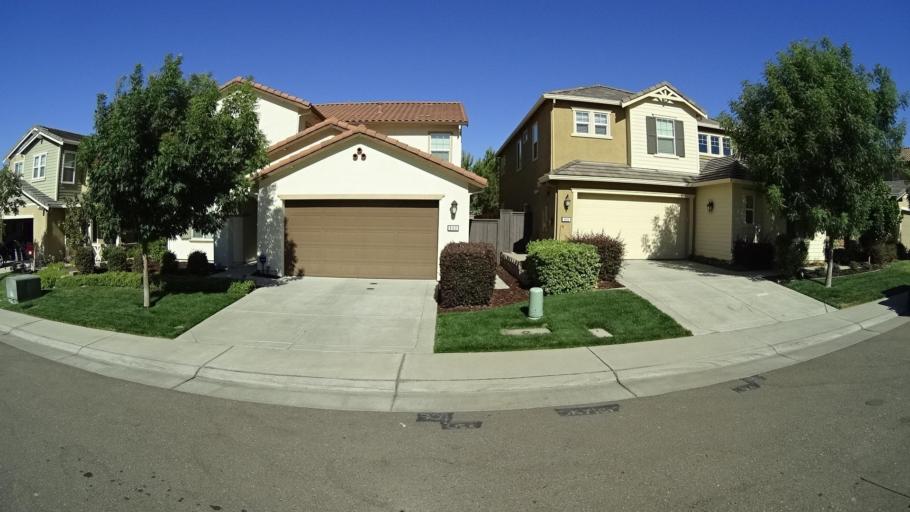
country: US
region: California
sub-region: Placer County
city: Lincoln
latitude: 38.8353
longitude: -121.2830
